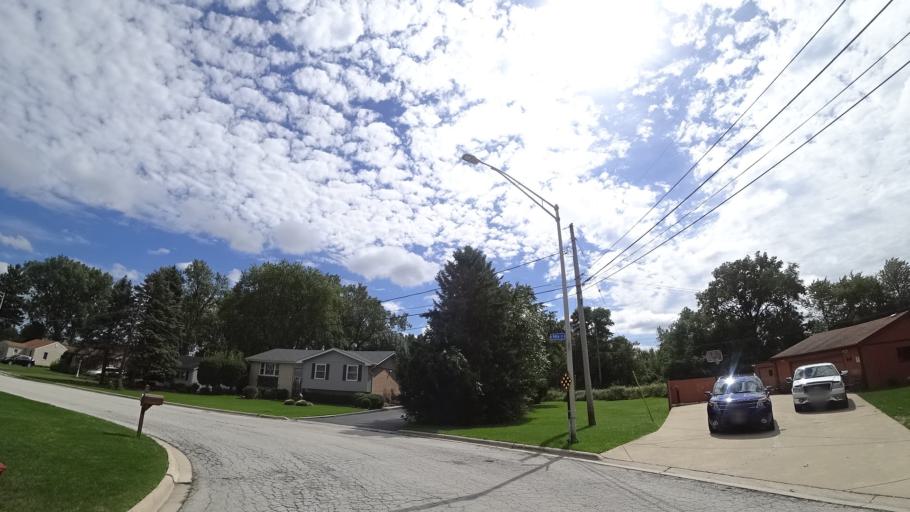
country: US
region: Illinois
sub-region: Cook County
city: Chicago Ridge
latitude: 41.7140
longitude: -87.7917
